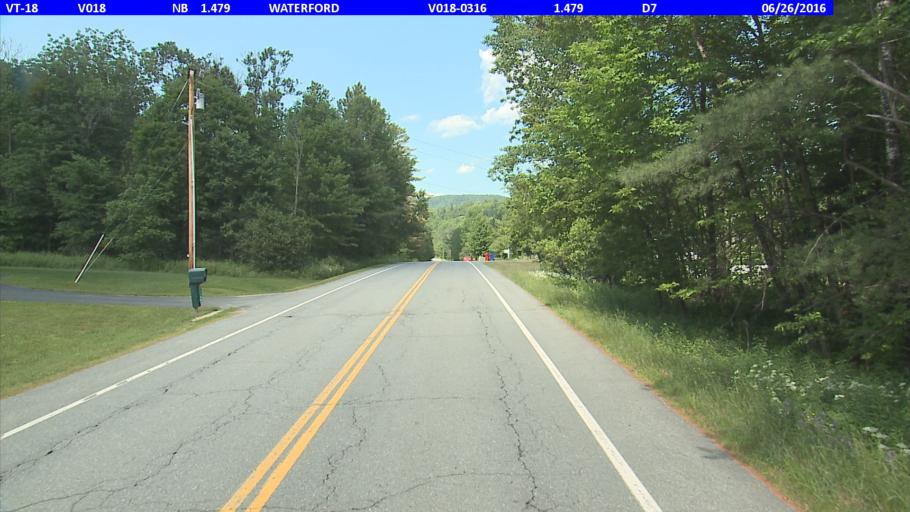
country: US
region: Vermont
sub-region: Caledonia County
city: Saint Johnsbury
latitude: 44.3583
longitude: -71.9064
